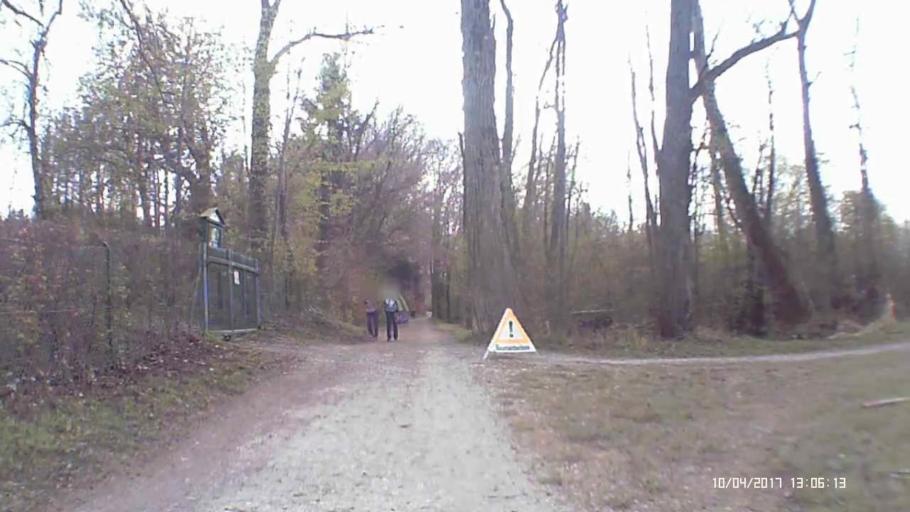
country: DE
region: Bavaria
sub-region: Upper Bavaria
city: Chieming
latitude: 47.9186
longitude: 12.4955
